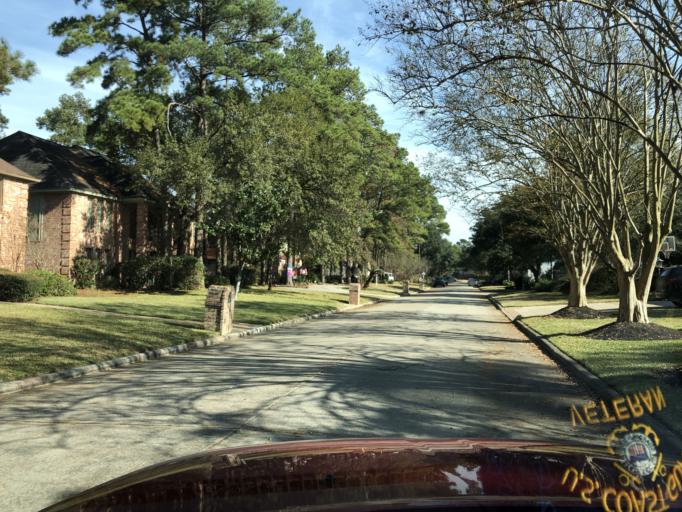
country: US
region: Texas
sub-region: Harris County
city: Tomball
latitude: 30.0293
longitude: -95.5558
